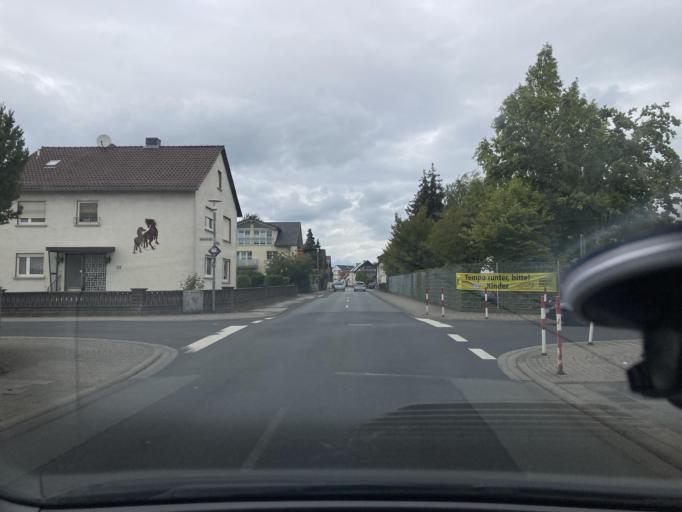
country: DE
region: Bavaria
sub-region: Regierungsbezirk Unterfranken
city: Kahl am Main
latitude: 50.0318
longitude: 9.0260
